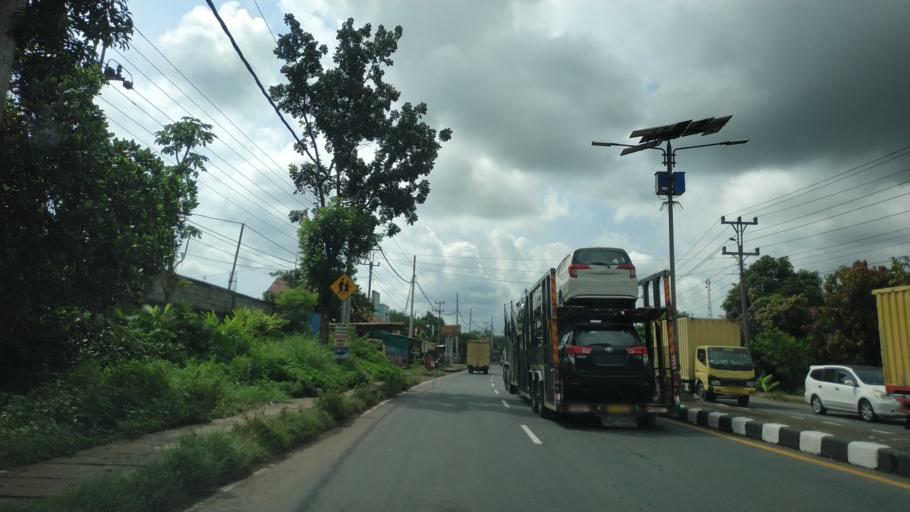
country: ID
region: Central Java
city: Pekalongan
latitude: -6.9476
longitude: 109.7831
